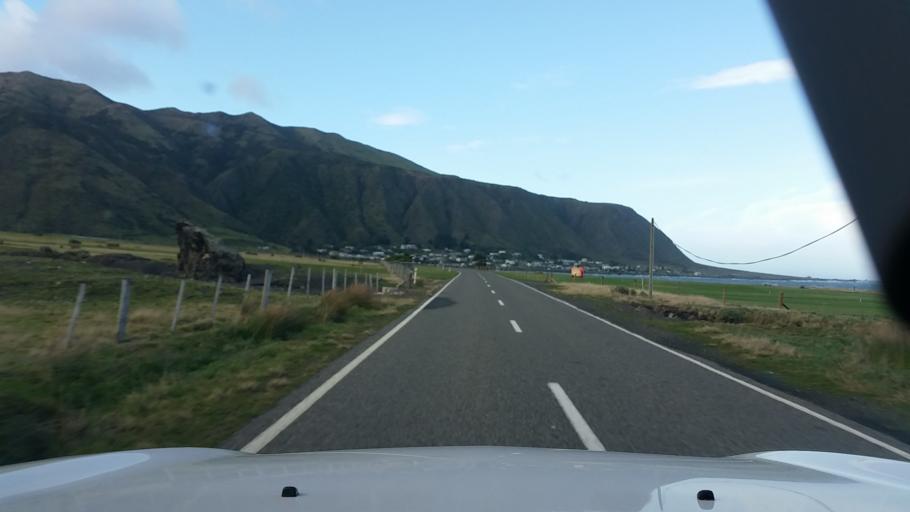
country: NZ
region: Wellington
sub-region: South Wairarapa District
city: Waipawa
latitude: -41.5788
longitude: 175.2265
